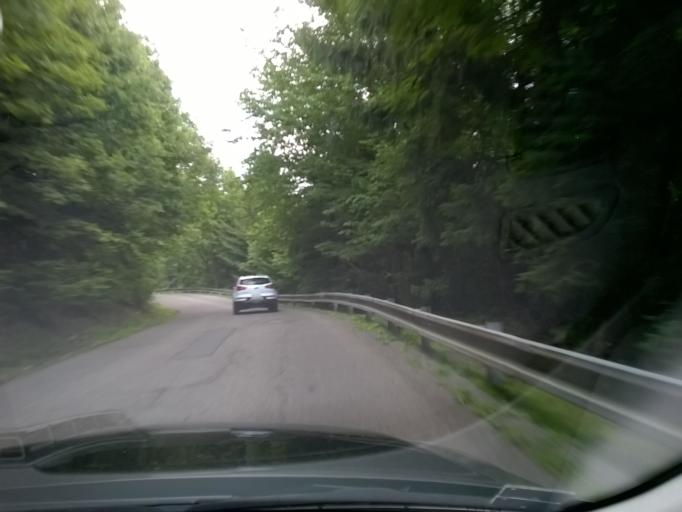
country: SK
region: Banskobystricky
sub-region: Okres Banska Bystrica
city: Banska Stiavnica
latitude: 48.4706
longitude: 18.8689
